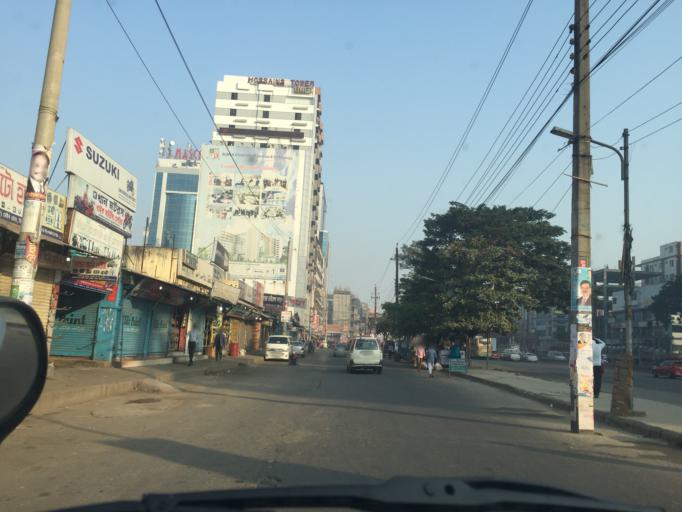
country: BD
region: Dhaka
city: Tungi
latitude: 23.8726
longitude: 90.4003
